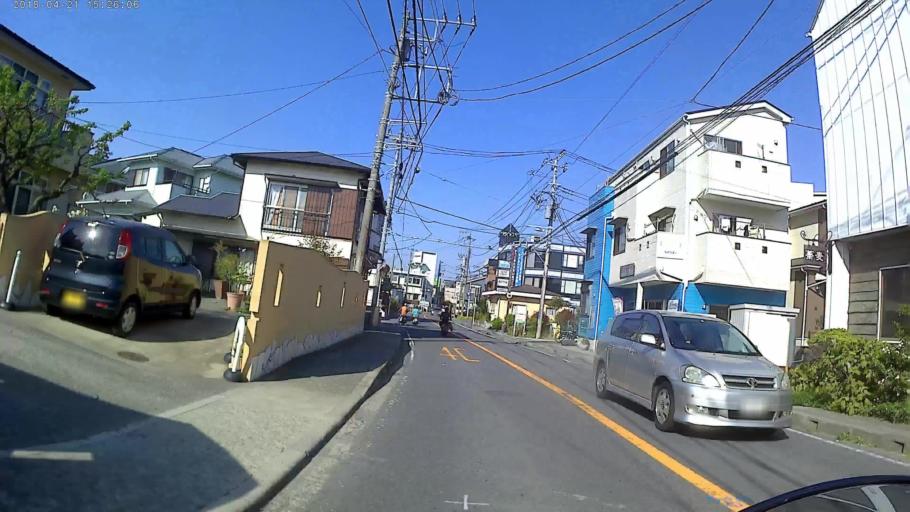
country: JP
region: Kanagawa
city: Fujisawa
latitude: 35.3104
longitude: 139.4958
